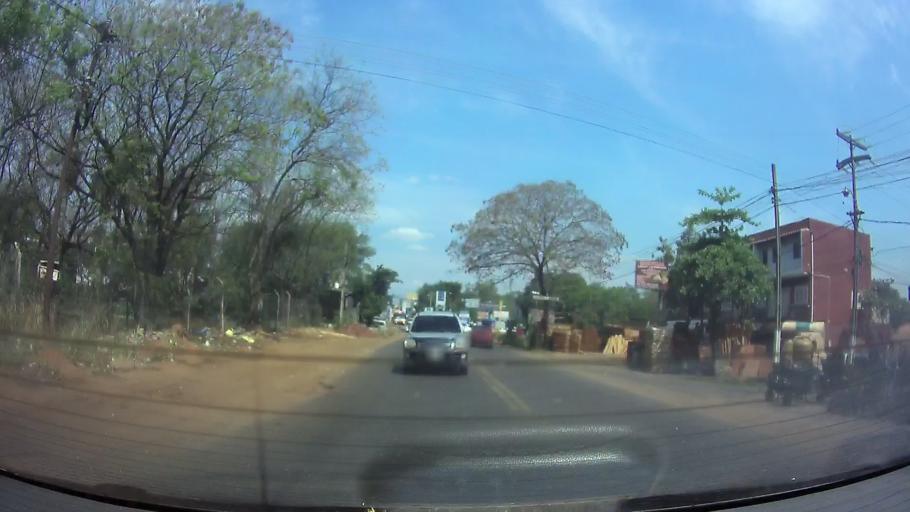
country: PY
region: Central
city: San Lorenzo
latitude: -25.3564
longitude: -57.4878
